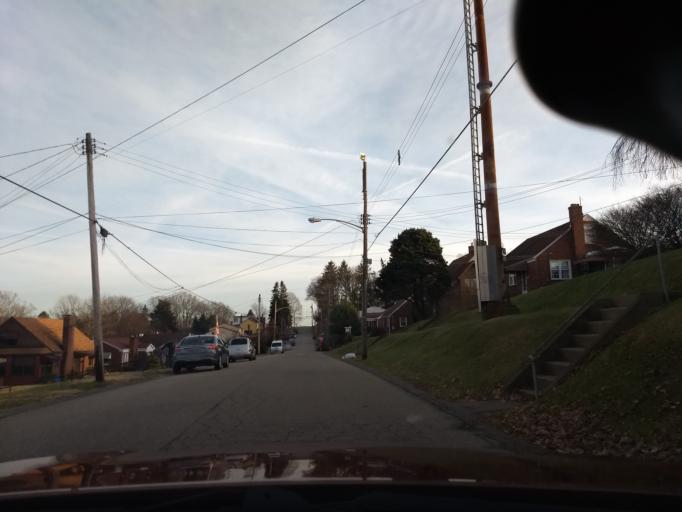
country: US
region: Pennsylvania
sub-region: Allegheny County
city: Dravosburg
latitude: 40.3545
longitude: -79.9097
